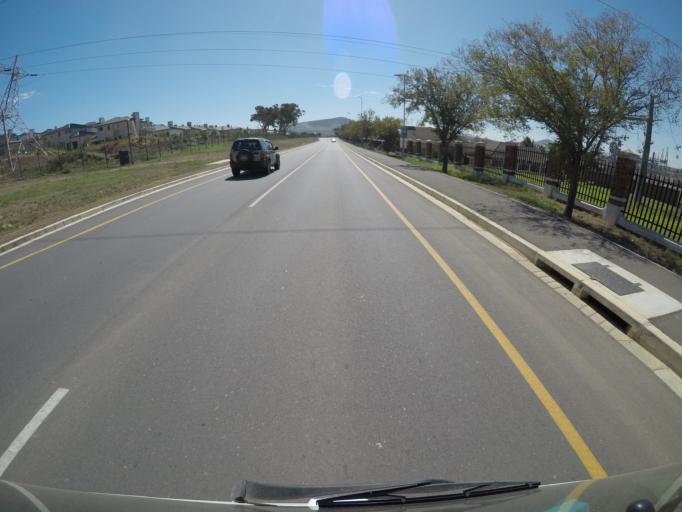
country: ZA
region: Western Cape
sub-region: City of Cape Town
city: Kraaifontein
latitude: -33.8225
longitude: 18.6363
